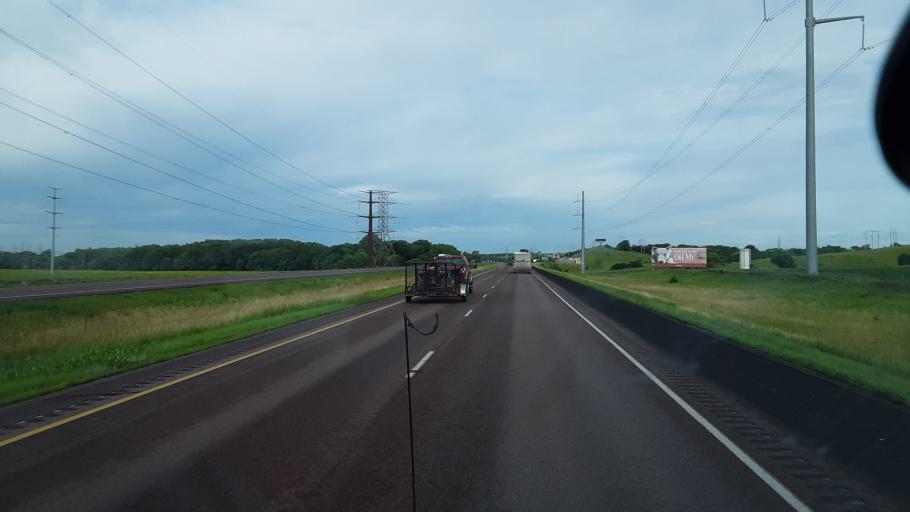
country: US
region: South Dakota
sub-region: Minnehaha County
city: Brandon
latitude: 43.6104
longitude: -96.6256
